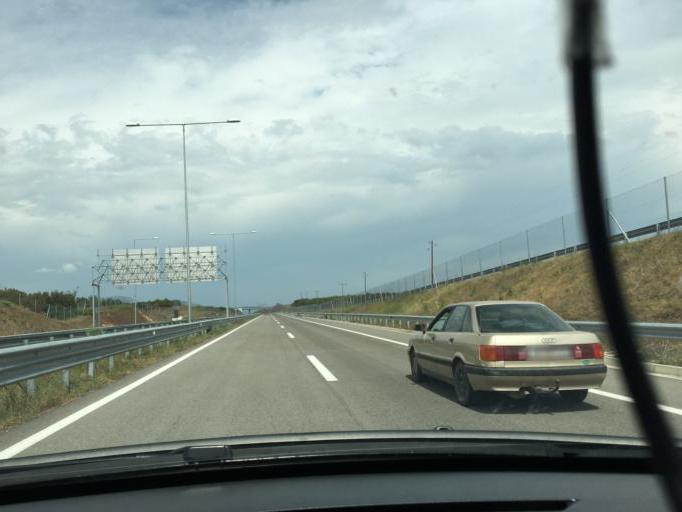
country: MK
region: Gevgelija
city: Miravci
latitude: 41.2664
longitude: 22.4693
